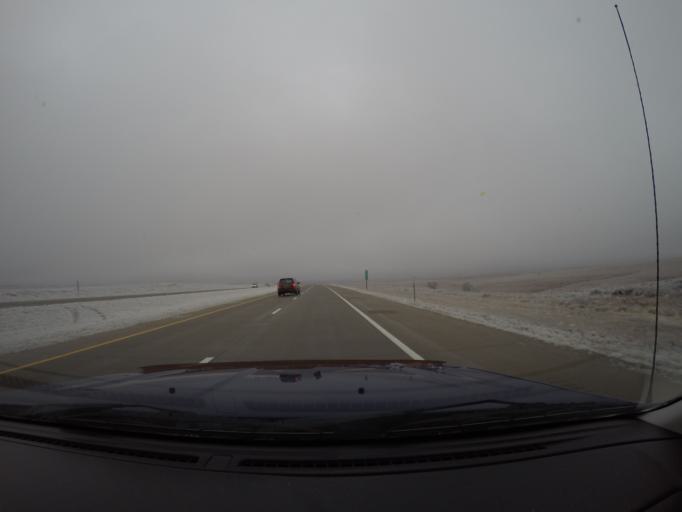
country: US
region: Kansas
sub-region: Wabaunsee County
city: Alma
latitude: 39.0653
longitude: -96.4275
